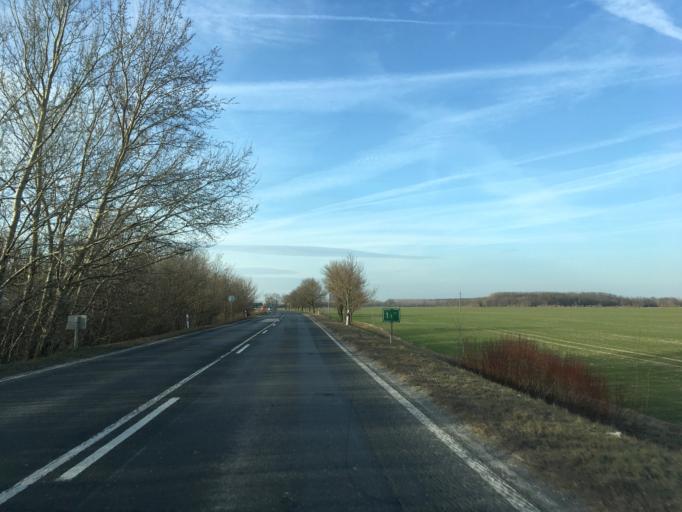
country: HU
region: Gyor-Moson-Sopron
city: Lebeny
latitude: 47.7774
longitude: 17.4184
